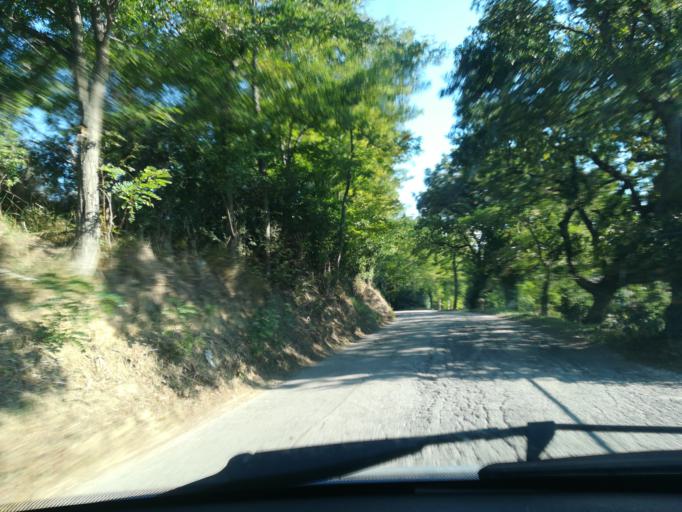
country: IT
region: The Marches
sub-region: Provincia di Macerata
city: Piediripa
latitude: 43.2997
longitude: 13.4799
